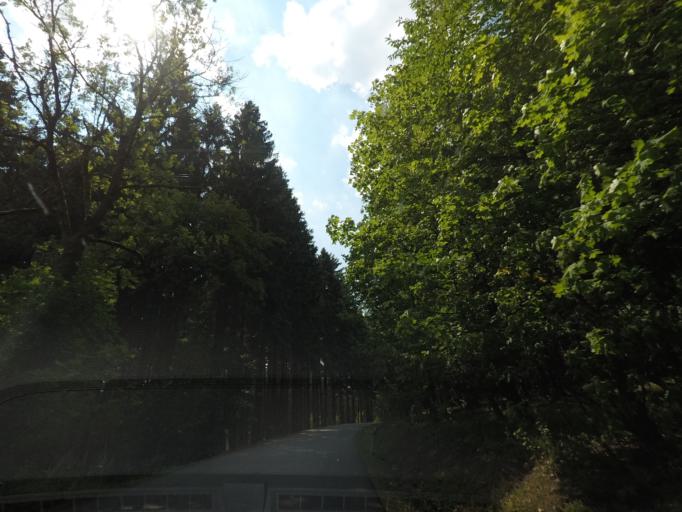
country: CZ
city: Radvanice
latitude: 50.6141
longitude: 16.0626
